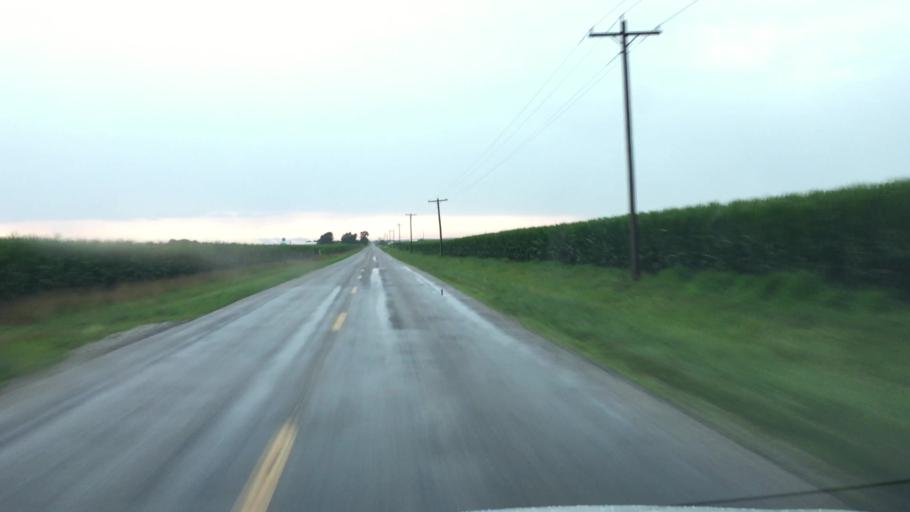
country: US
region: Iowa
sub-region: Lee County
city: Fort Madison
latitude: 40.5209
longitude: -91.2547
